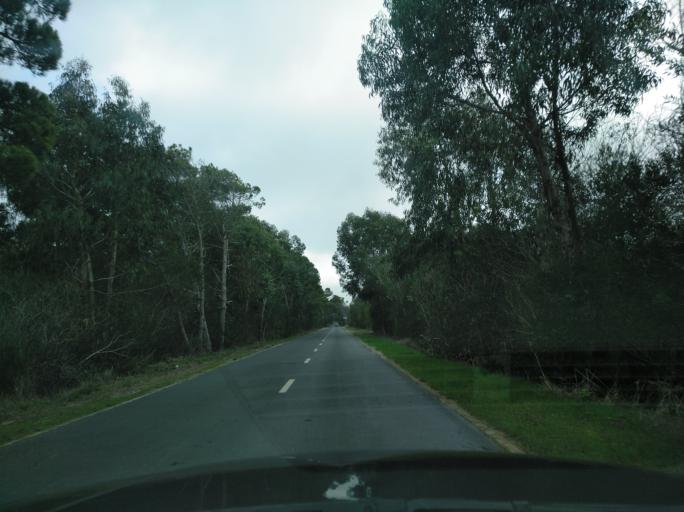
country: PT
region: Beja
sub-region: Odemira
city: Vila Nova de Milfontes
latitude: 37.7138
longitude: -8.7792
